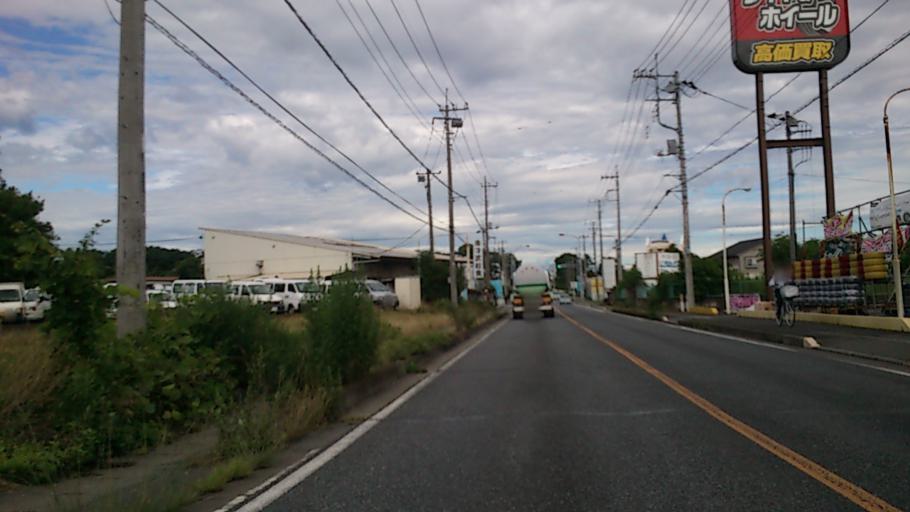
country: JP
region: Saitama
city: Honjo
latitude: 36.2502
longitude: 139.1783
